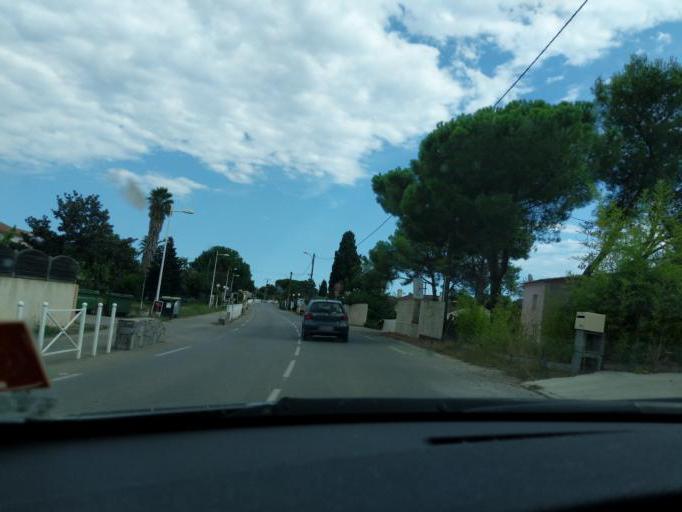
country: FR
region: Corsica
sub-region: Departement de la Haute-Corse
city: Ghisonaccia
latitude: 42.0093
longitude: 9.4126
